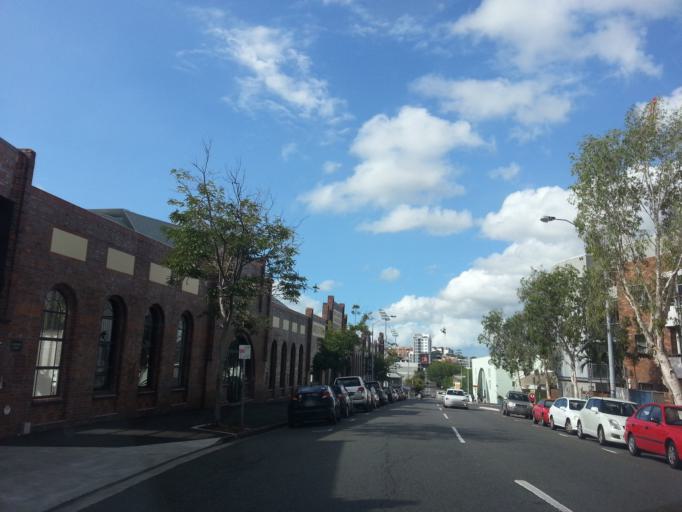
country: AU
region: Queensland
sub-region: Brisbane
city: Fortitude Valley
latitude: -27.4519
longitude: 153.0305
